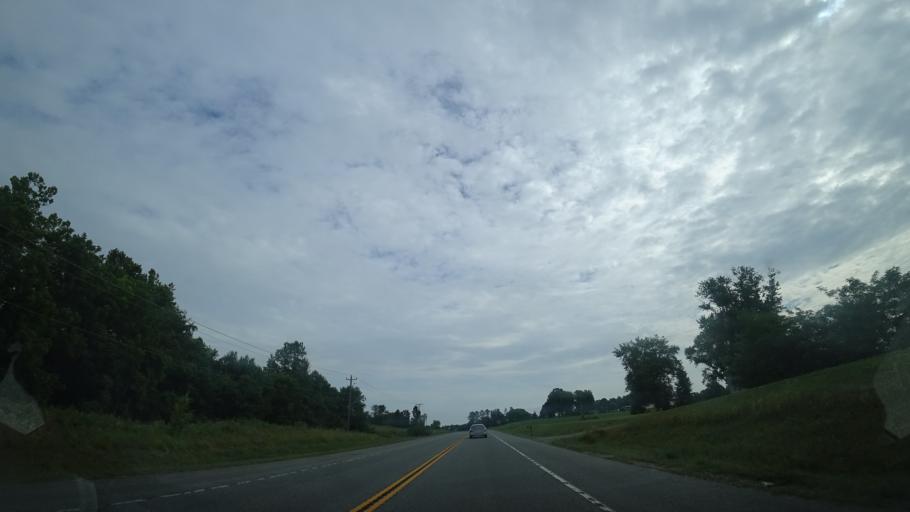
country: US
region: Virginia
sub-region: Spotsylvania County
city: Spotsylvania Courthouse
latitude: 38.1831
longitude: -77.6217
